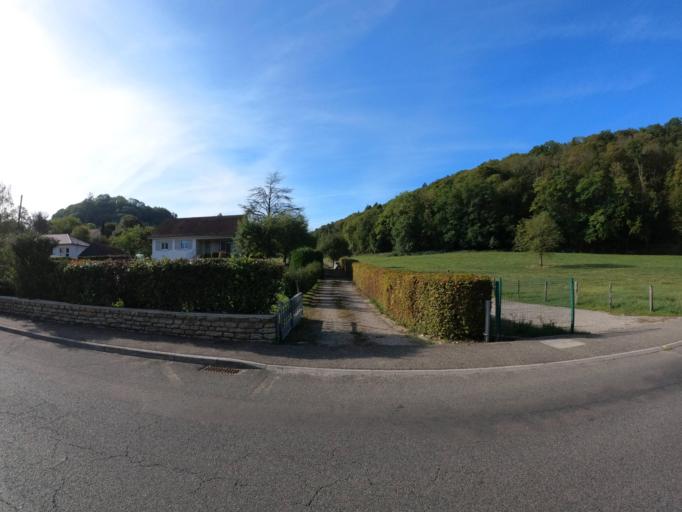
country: FR
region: Franche-Comte
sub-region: Departement du Jura
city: Montmorot
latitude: 46.7183
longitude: 5.5284
